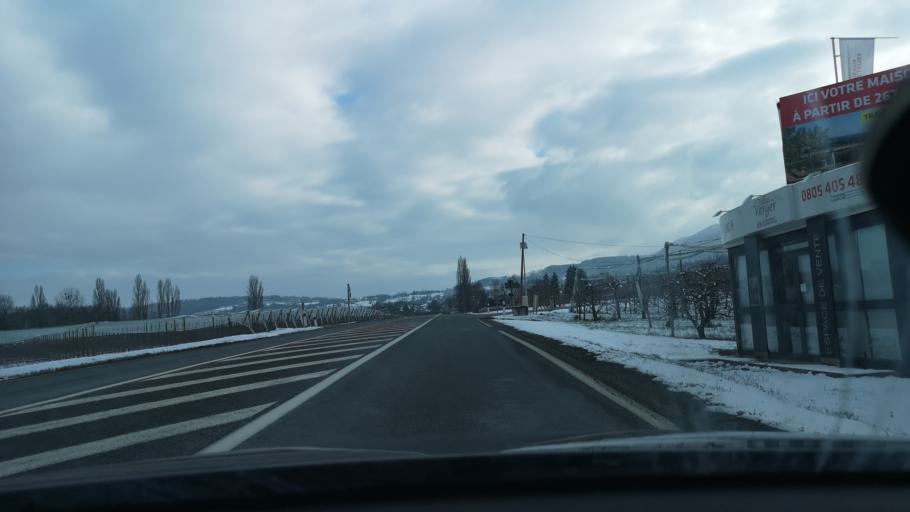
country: FR
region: Rhone-Alpes
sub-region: Departement de l'Ain
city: Collonges
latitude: 46.1131
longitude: 5.9197
